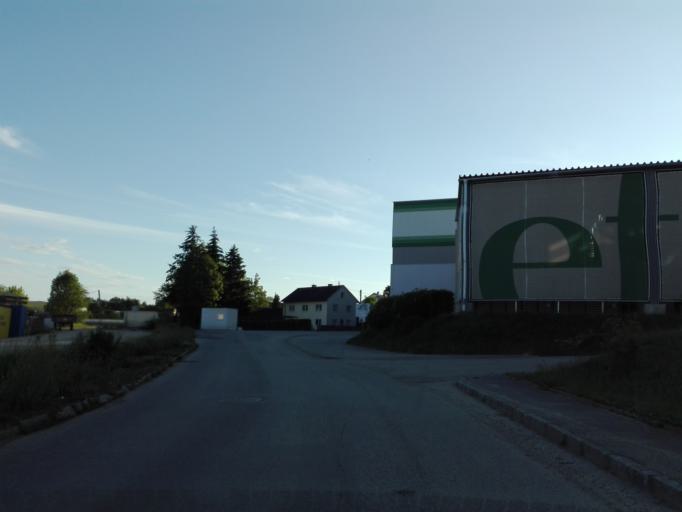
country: AT
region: Upper Austria
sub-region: Politischer Bezirk Urfahr-Umgebung
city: Feldkirchen an der Donau
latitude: 48.3104
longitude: 14.0047
